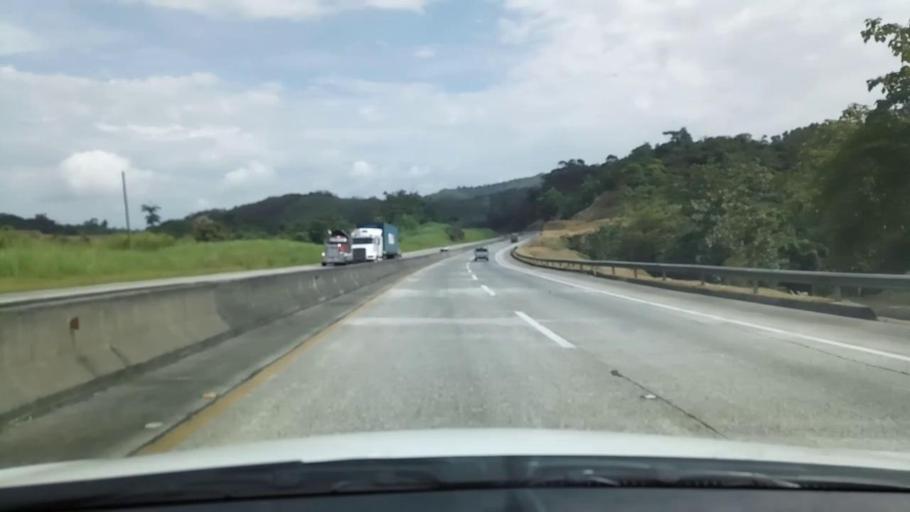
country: PA
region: Colon
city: Quebrada Bonita Adentro
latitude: 9.2792
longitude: -79.7271
